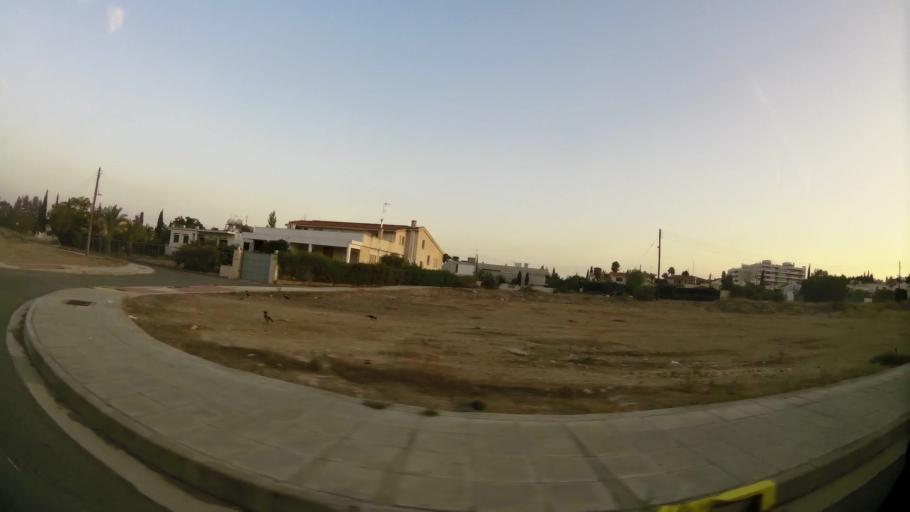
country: CY
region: Lefkosia
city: Nicosia
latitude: 35.1565
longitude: 33.3236
